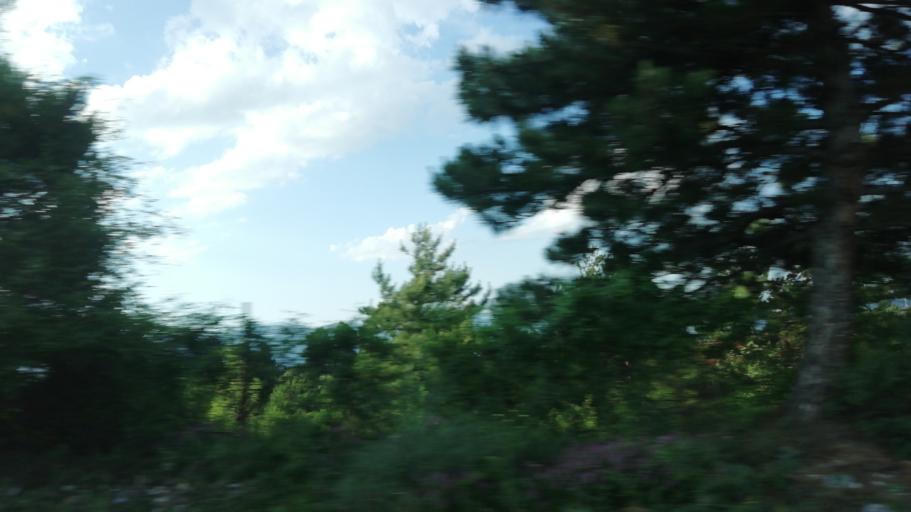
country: TR
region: Karabuk
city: Karabuk
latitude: 41.1285
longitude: 32.6094
